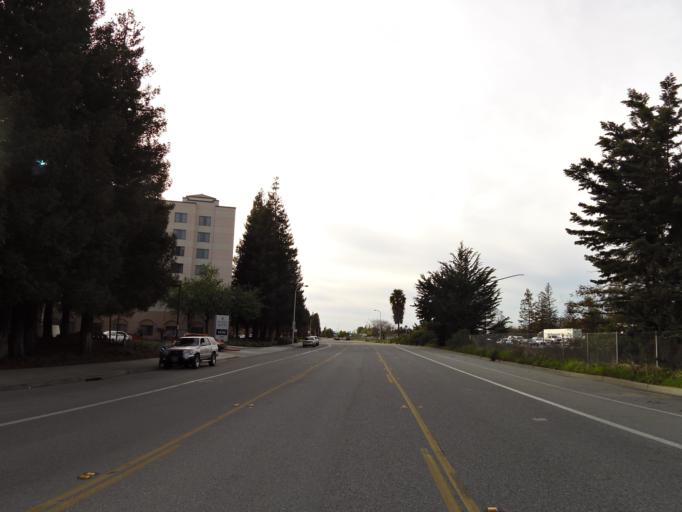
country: US
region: California
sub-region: Santa Clara County
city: Santa Clara
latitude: 37.3868
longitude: -121.9824
